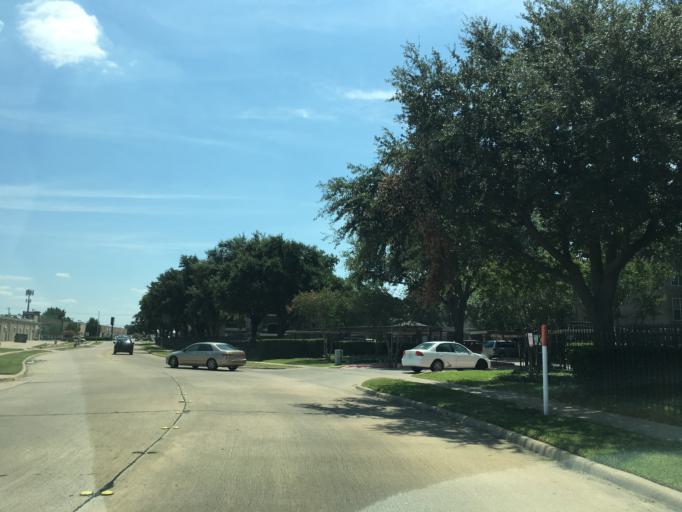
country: US
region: Texas
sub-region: Denton County
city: Lewisville
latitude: 33.0246
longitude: -96.9954
